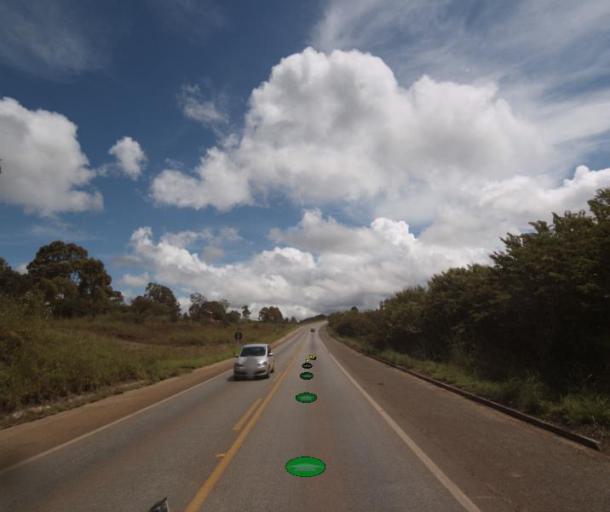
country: BR
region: Federal District
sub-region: Brasilia
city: Brasilia
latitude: -15.7433
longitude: -48.3684
